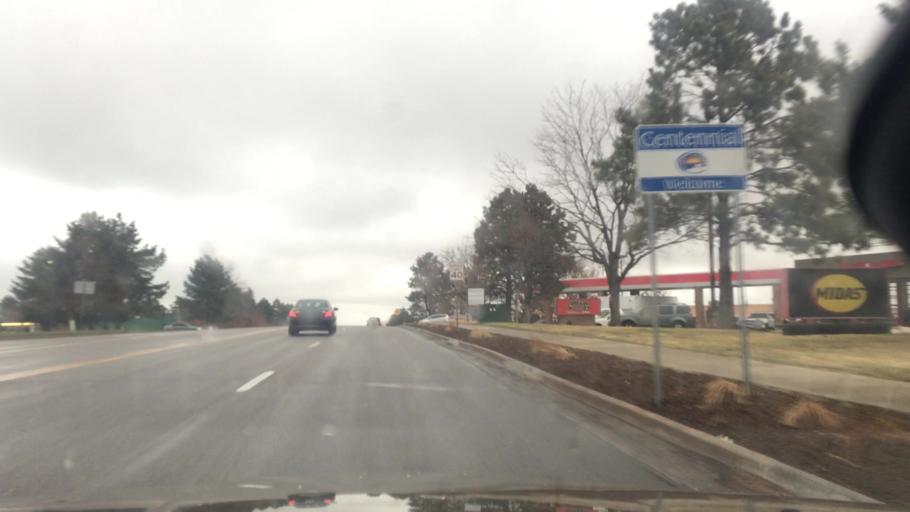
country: US
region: Colorado
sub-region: Arapahoe County
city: Castlewood
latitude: 39.5664
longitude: -104.9230
